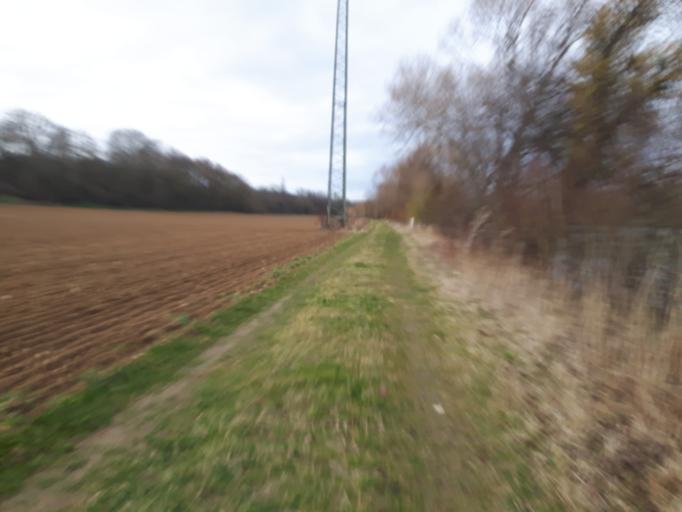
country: DE
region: Baden-Wuerttemberg
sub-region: Regierungsbezirk Stuttgart
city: Neckarwestheim
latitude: 49.0483
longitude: 9.1722
